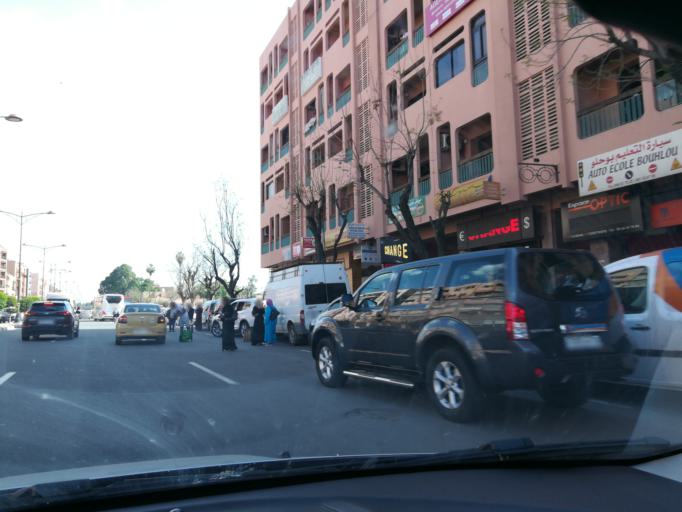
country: MA
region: Marrakech-Tensift-Al Haouz
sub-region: Marrakech
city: Marrakesh
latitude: 31.6364
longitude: -8.0176
